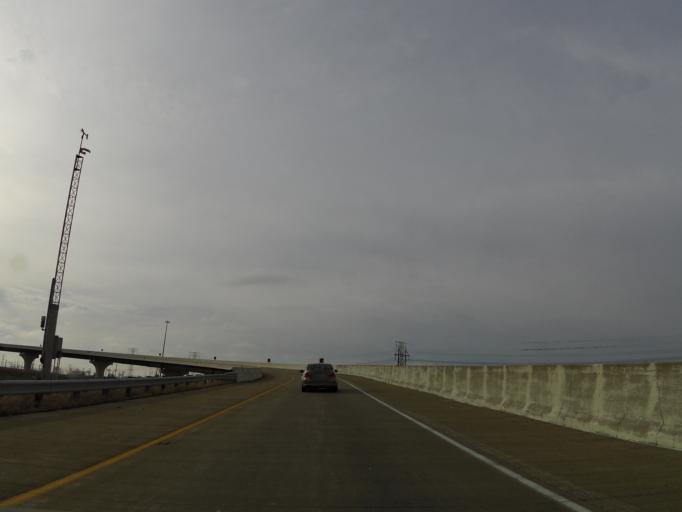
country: US
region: Indiana
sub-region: Marion County
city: Beech Grove
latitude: 39.7339
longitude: -86.0459
